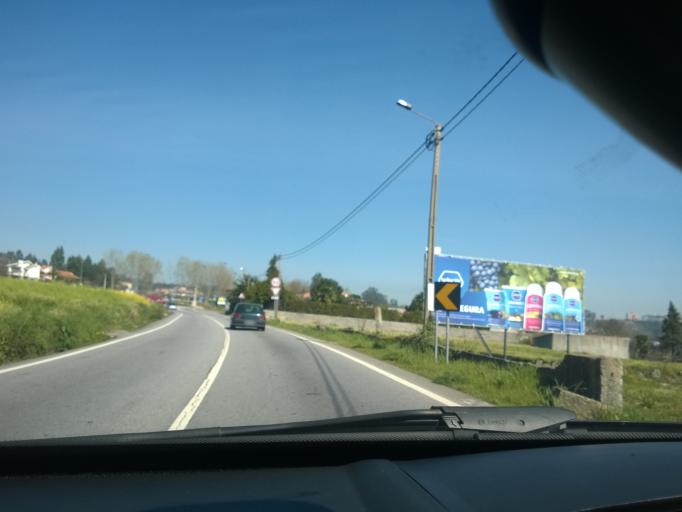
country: PT
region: Porto
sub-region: Paredes
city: Paredes
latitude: 41.1815
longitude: -8.3066
